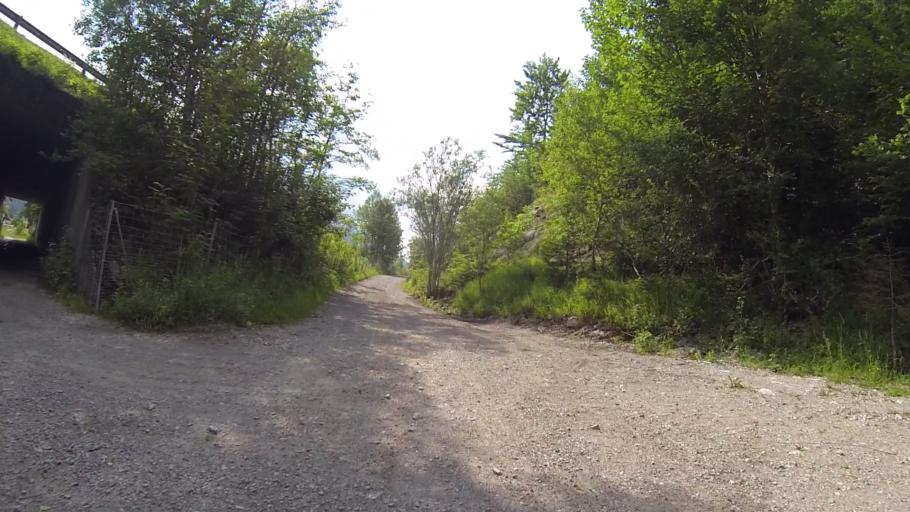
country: AT
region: Tyrol
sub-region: Politischer Bezirk Reutte
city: Pflach
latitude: 47.5212
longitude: 10.7174
